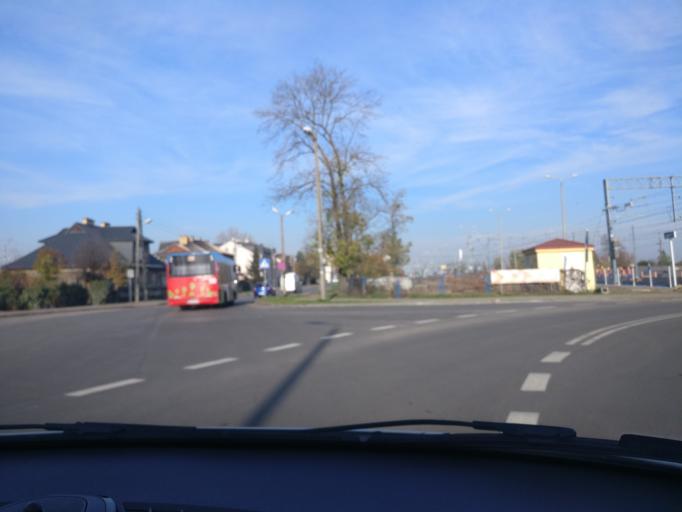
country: PL
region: Lublin Voivodeship
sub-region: Powiat rycki
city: Deblin
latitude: 51.5757
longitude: 21.8375
